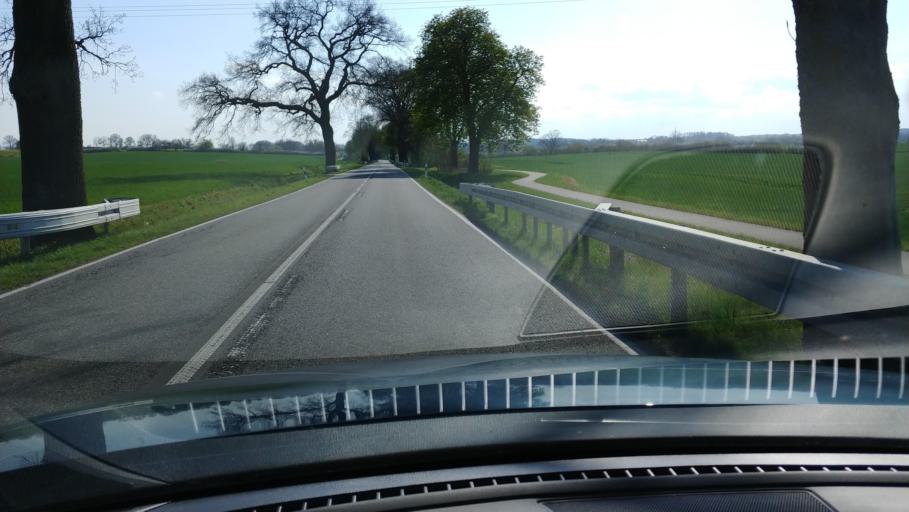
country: DE
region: Mecklenburg-Vorpommern
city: Muhlen Eichsen
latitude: 53.7723
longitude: 11.2714
